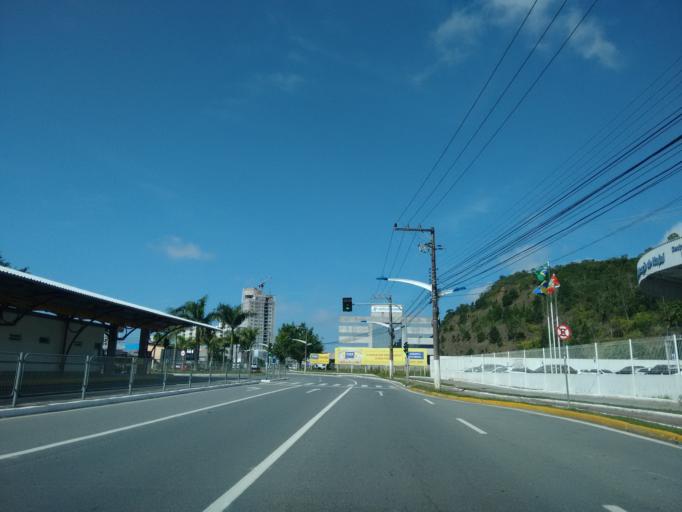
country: BR
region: Santa Catarina
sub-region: Itajai
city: Itajai
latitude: -26.9298
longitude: -48.6847
